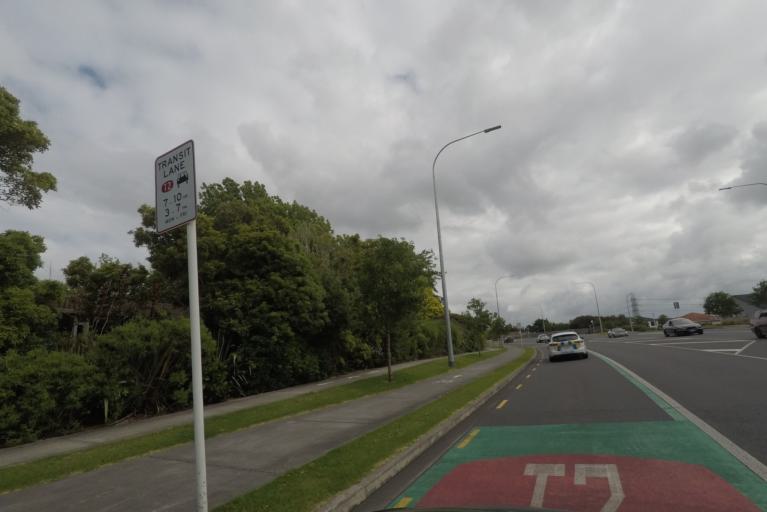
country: NZ
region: Auckland
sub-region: Auckland
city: Rothesay Bay
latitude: -36.7341
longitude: 174.6917
